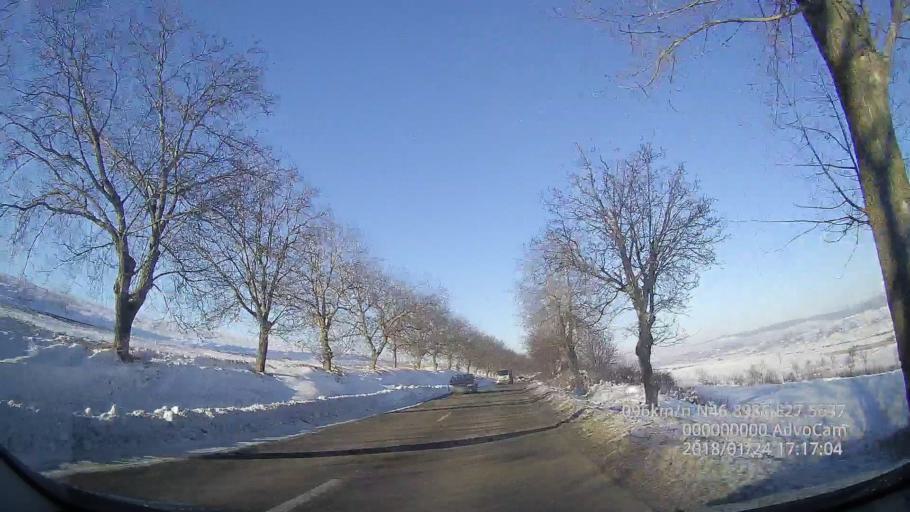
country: RO
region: Iasi
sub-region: Comuna Scanteia
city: Scanteia
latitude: 46.8994
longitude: 27.5637
